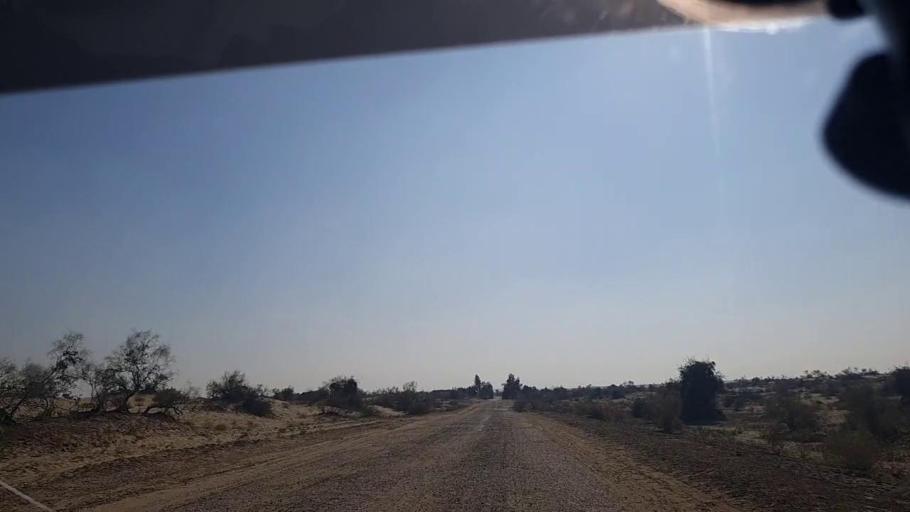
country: PK
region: Sindh
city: Khanpur
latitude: 27.5712
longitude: 69.3052
